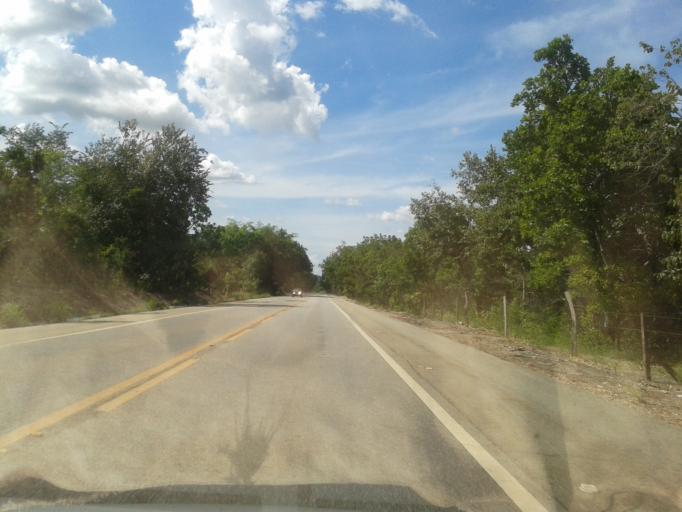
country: BR
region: Goias
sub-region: Itapuranga
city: Itapuranga
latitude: -15.5012
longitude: -50.3056
